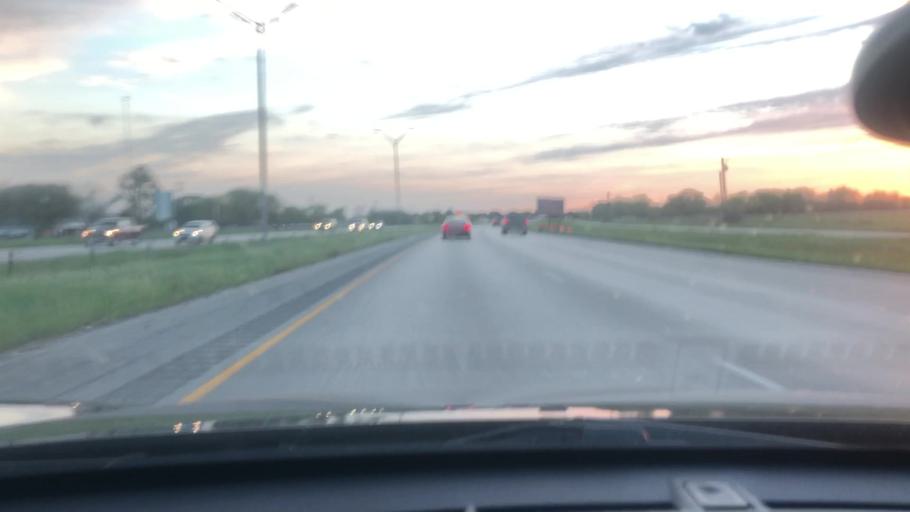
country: US
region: Texas
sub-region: Jackson County
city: Edna
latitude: 28.9639
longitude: -96.6760
